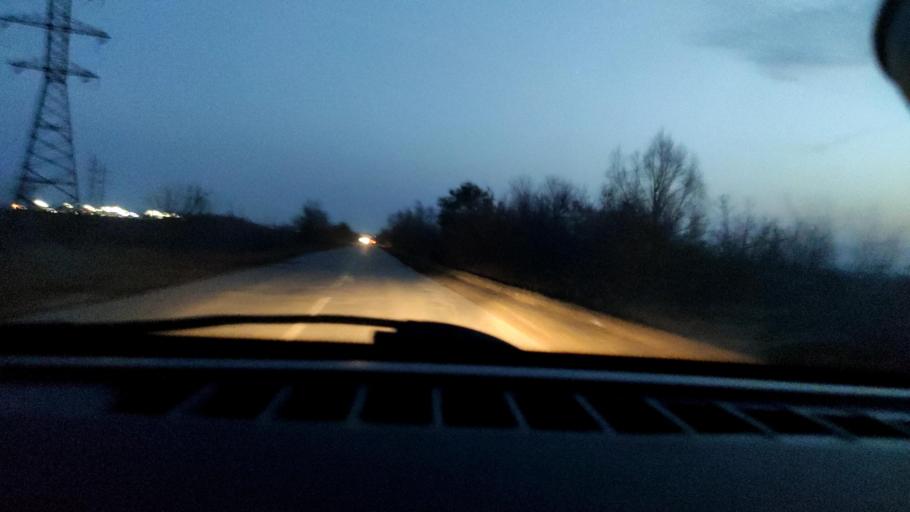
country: RU
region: Samara
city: Samara
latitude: 53.1143
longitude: 50.2241
